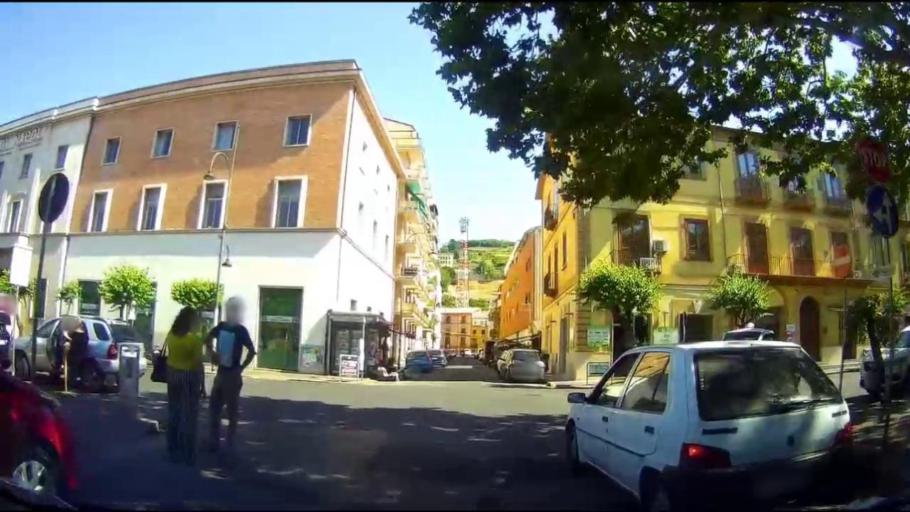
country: IT
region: Calabria
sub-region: Provincia di Cosenza
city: Cosenza
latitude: 39.2940
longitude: 16.2545
